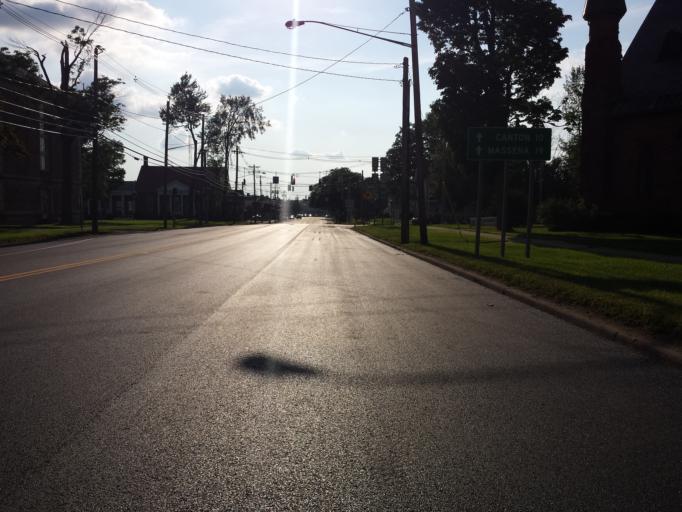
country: US
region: New York
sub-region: St. Lawrence County
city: Potsdam
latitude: 44.6699
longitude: -74.9806
